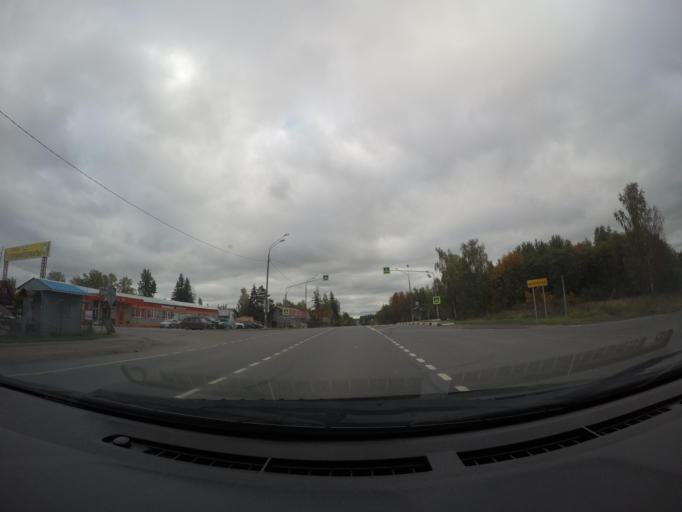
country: RU
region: Moskovskaya
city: Dorokhovo
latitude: 55.6223
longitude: 36.3430
